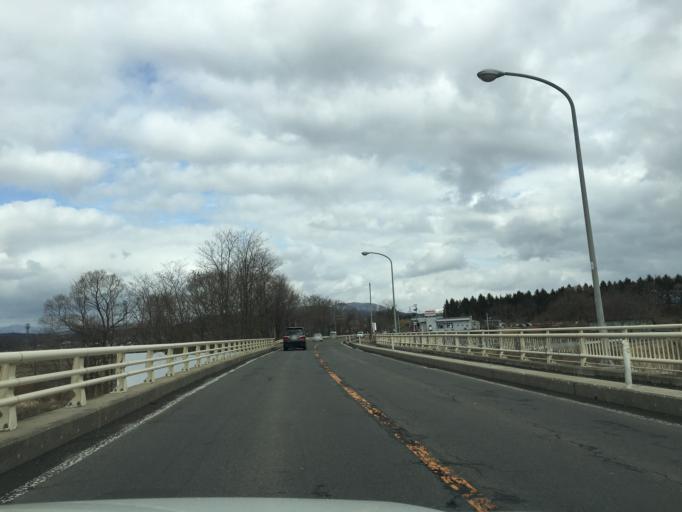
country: JP
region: Akita
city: Hanawa
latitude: 40.2600
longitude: 140.7637
